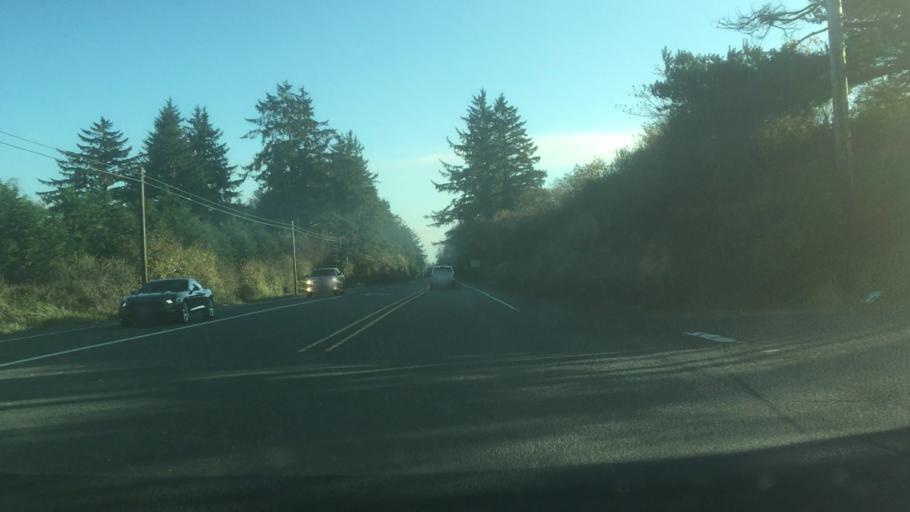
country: US
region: Oregon
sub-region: Clatsop County
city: Gearhart
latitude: 46.0582
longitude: -123.9154
